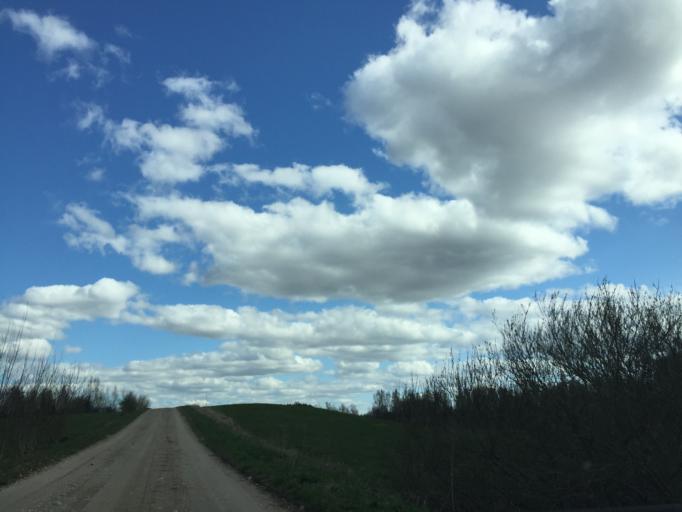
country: LV
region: Rezekne
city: Rezekne
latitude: 56.6646
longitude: 27.2915
